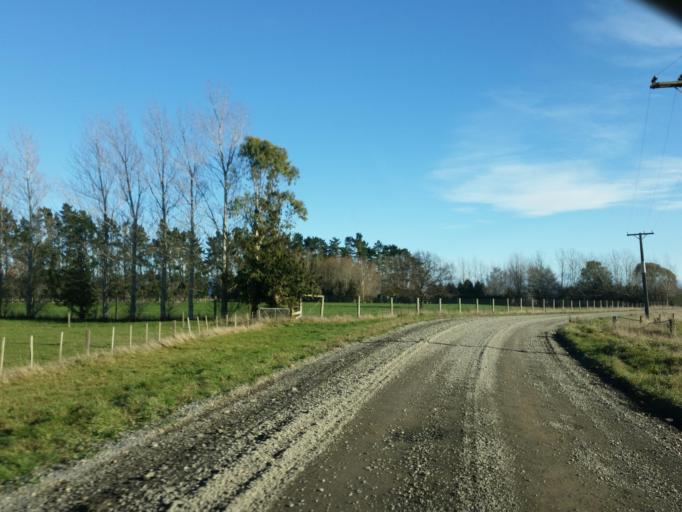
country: NZ
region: Southland
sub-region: Southland District
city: Winton
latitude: -46.0989
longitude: 168.1159
